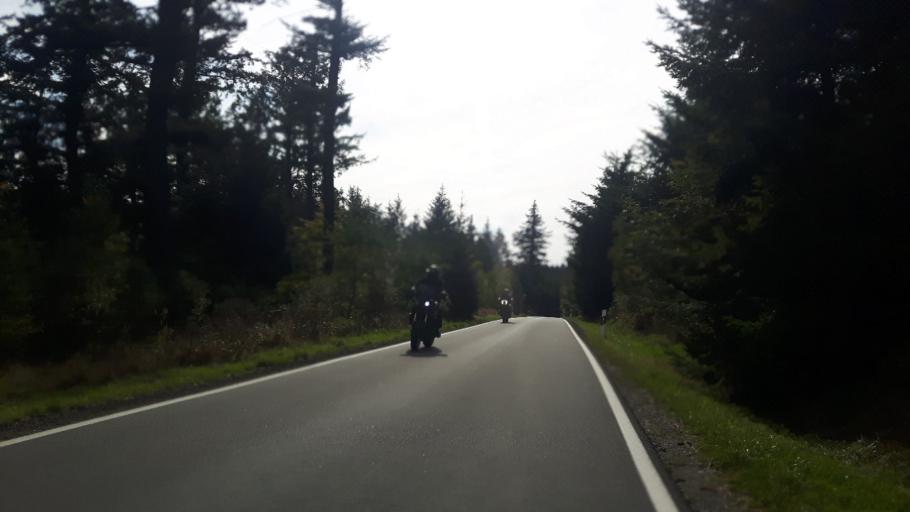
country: DE
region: North Rhine-Westphalia
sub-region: Regierungsbezirk Arnsberg
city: Erndtebruck
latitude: 50.9044
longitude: 8.2452
